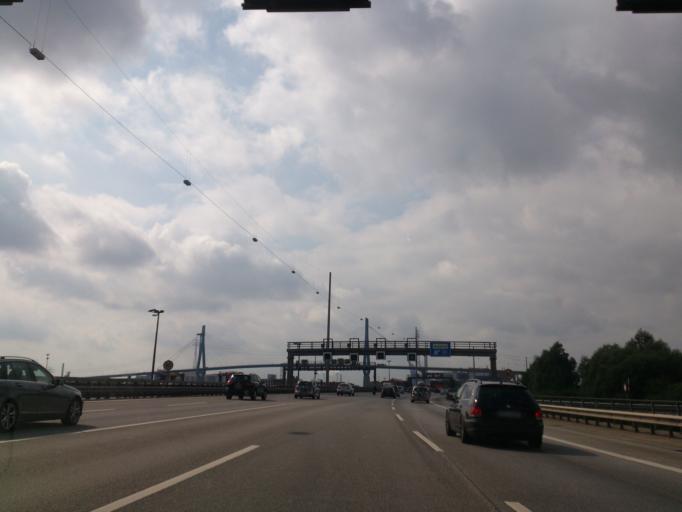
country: DE
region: Hamburg
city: Altona
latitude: 53.5323
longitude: 9.9334
